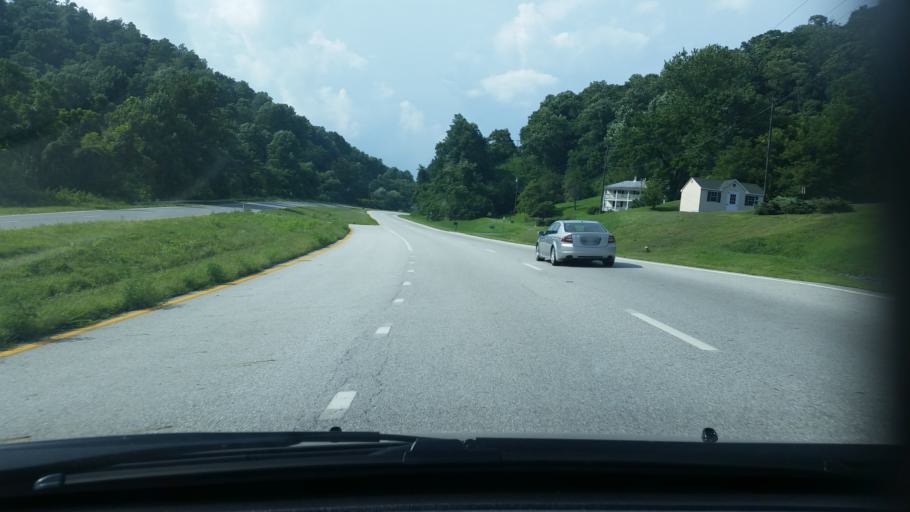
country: US
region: Virginia
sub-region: Nelson County
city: Lovingston
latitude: 37.7689
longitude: -78.8694
